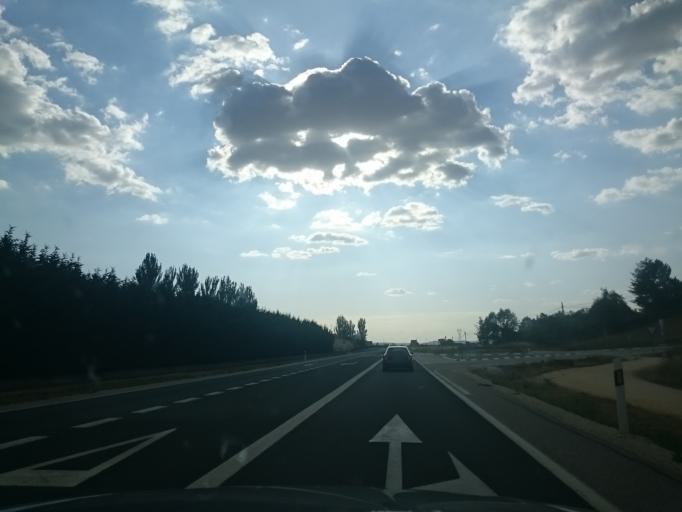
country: ES
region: Castille and Leon
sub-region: Provincia de Burgos
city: Los Tomillares
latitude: 42.3339
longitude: -3.5695
